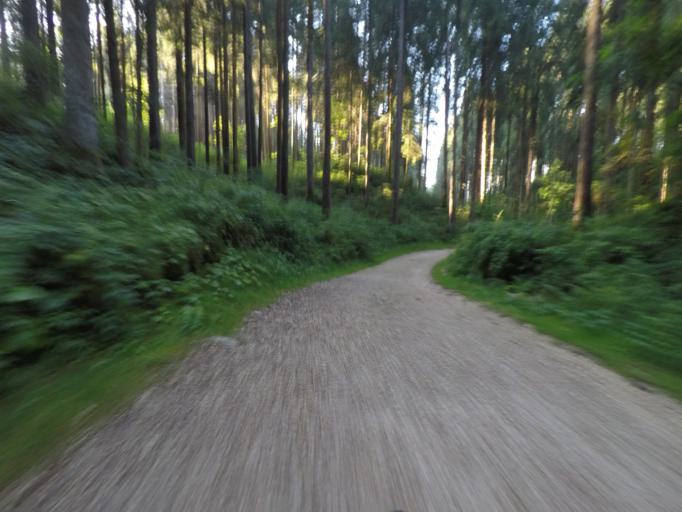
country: IT
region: Veneto
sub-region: Provincia di Vicenza
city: Asiago
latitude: 45.8598
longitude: 11.5275
